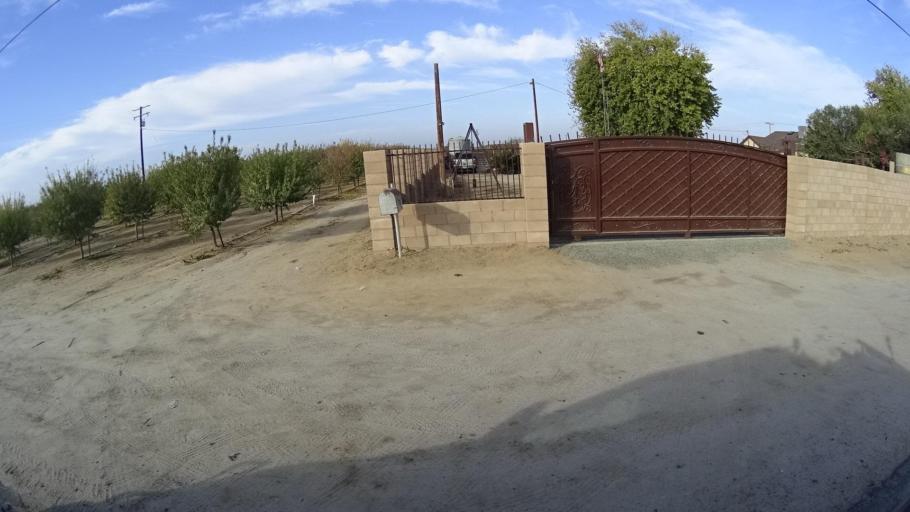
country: US
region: California
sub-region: Kern County
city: Delano
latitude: 35.7608
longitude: -119.2053
